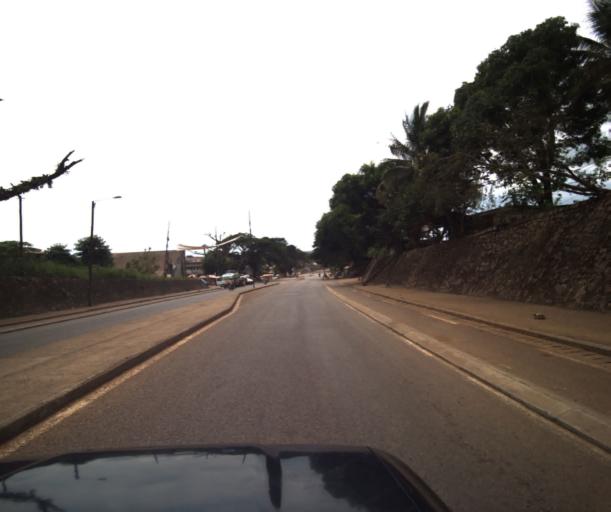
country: CM
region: Littoral
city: Edea
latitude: 3.7920
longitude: 10.1355
